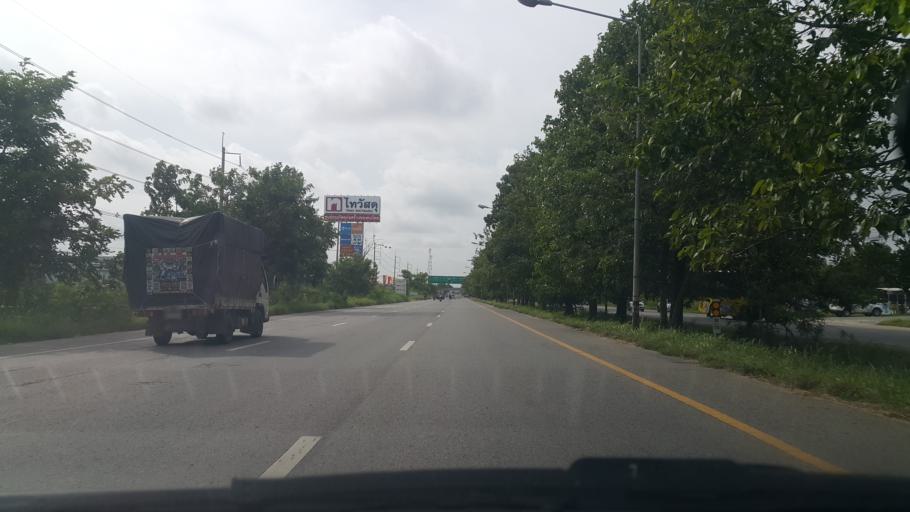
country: TH
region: Rayong
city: Rayong
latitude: 12.6690
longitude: 101.3065
